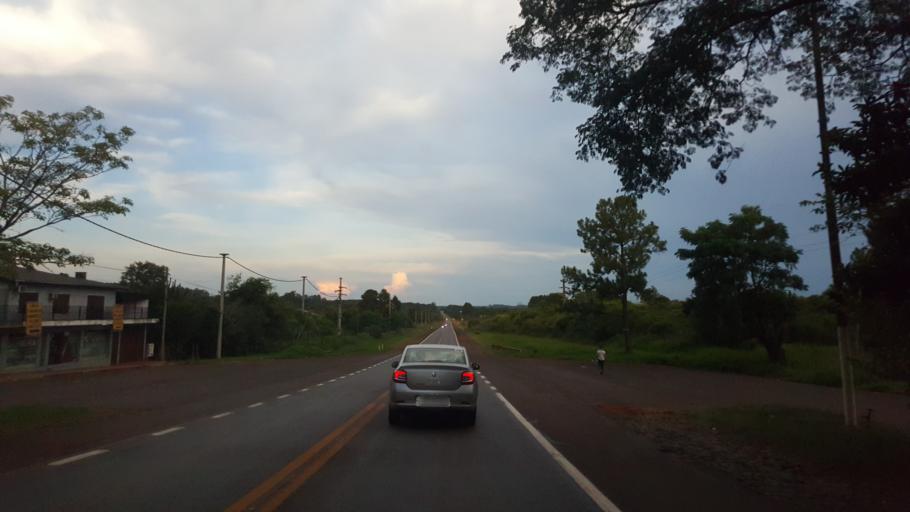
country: AR
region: Misiones
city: Jardin America
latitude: -27.0333
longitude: -55.2227
